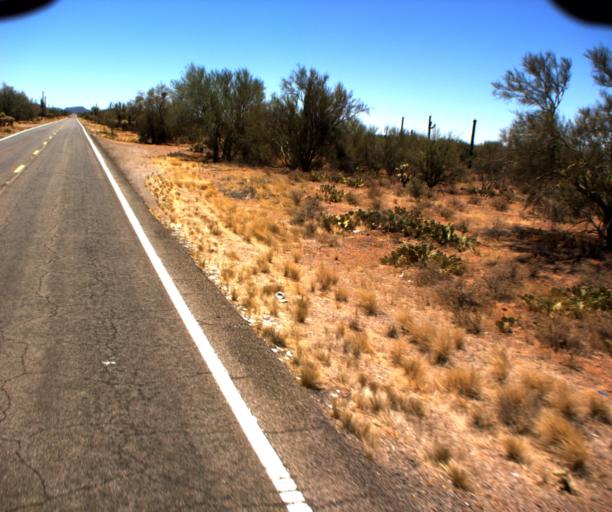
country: US
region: Arizona
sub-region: Pima County
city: Sells
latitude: 32.0484
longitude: -112.0240
